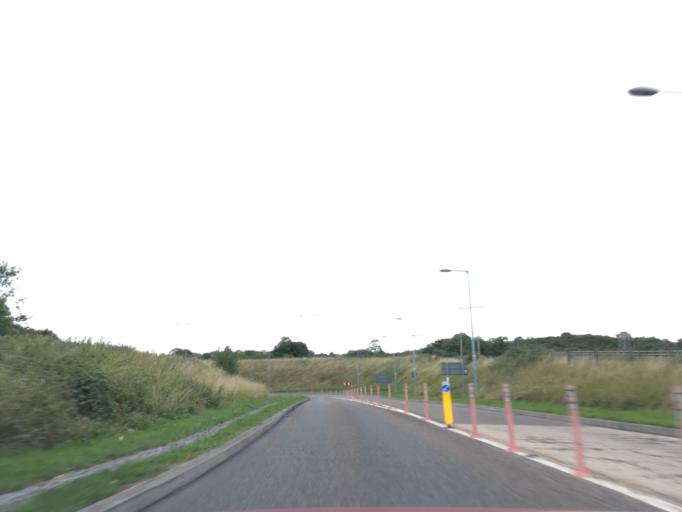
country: IE
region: Munster
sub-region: An Clar
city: Ennis
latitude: 52.8603
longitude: -8.9343
